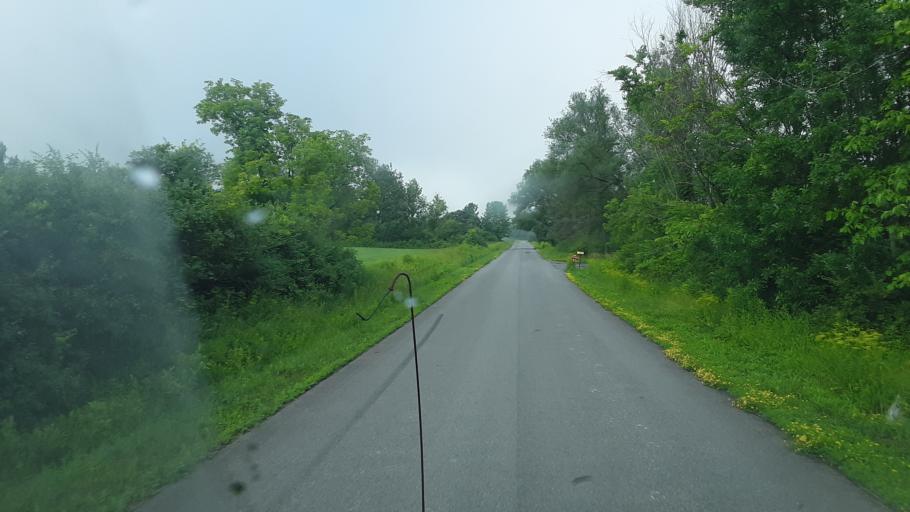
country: US
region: New York
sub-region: Montgomery County
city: Fonda
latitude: 42.9113
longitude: -74.3866
